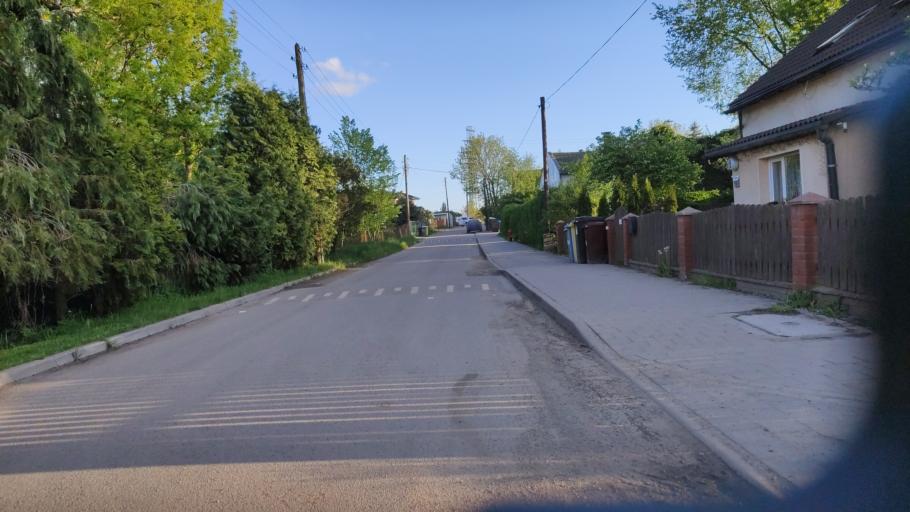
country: PL
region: Lower Silesian Voivodeship
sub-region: Powiat wroclawski
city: Zerniki Wroclawskie
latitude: 51.0475
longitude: 17.0528
